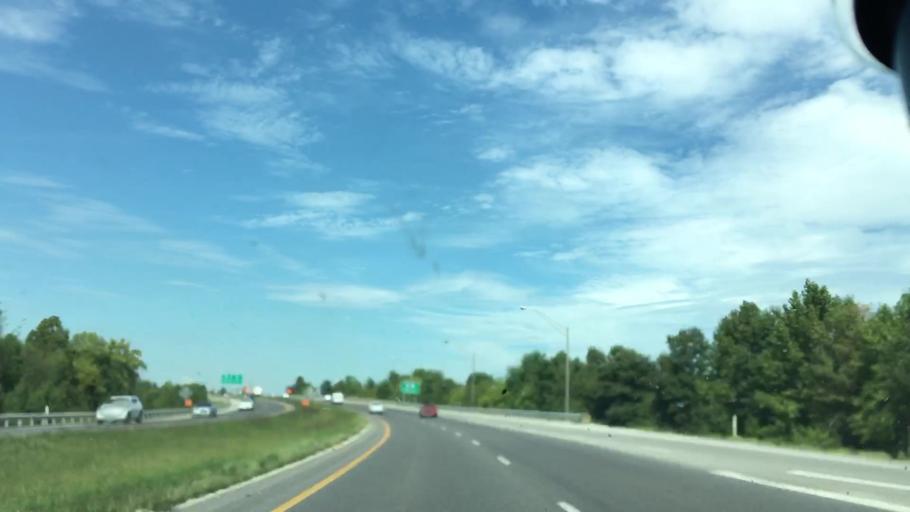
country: US
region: Kentucky
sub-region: Daviess County
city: Owensboro
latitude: 37.7421
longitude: -87.0720
